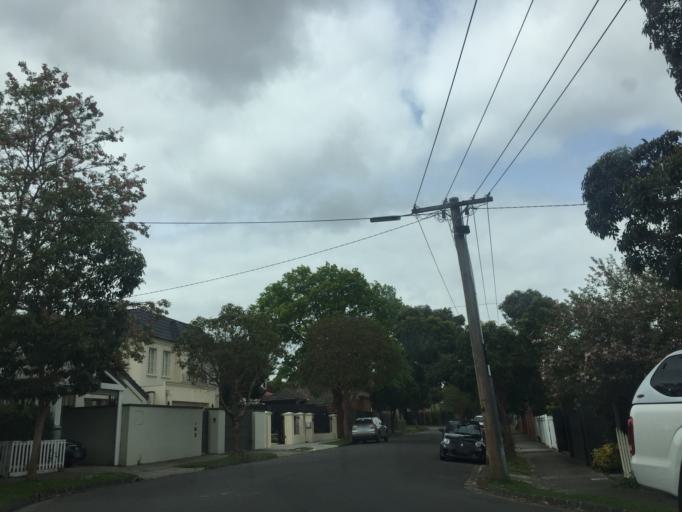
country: AU
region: Victoria
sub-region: Boroondara
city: Kew East
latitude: -37.8027
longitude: 145.0535
